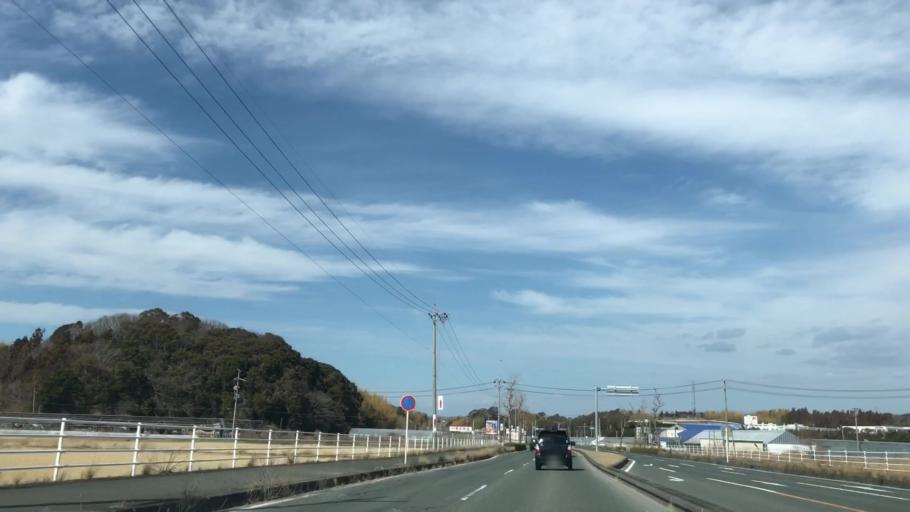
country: JP
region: Shizuoka
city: Hamamatsu
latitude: 34.7050
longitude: 137.6486
